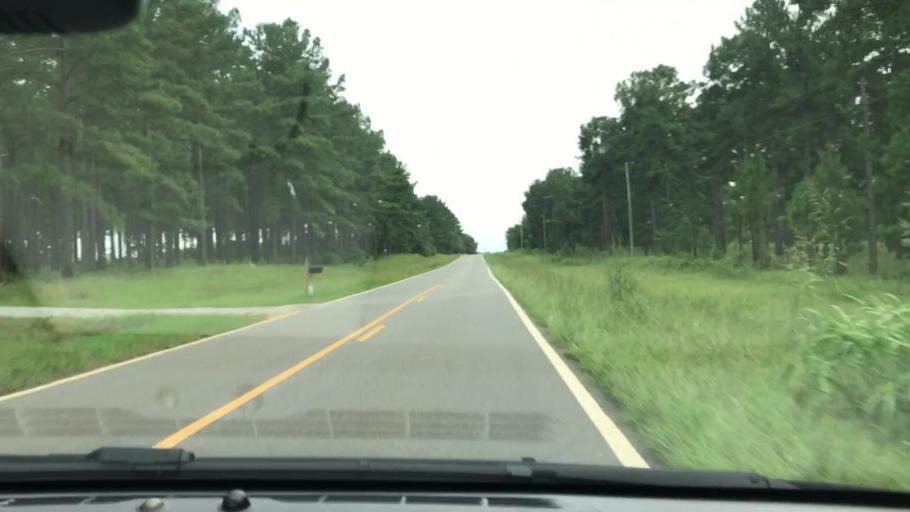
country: US
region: Georgia
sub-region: Early County
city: Blakely
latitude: 31.4567
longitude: -84.9166
